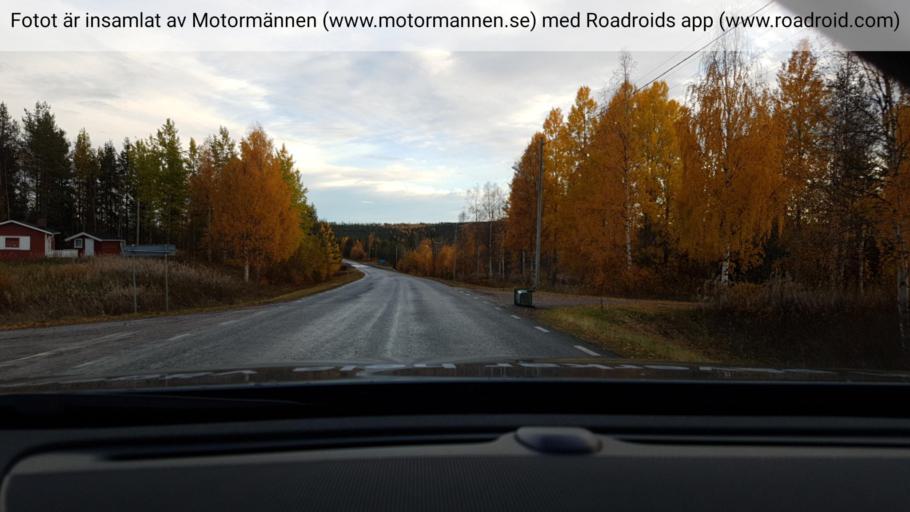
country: SE
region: Norrbotten
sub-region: Overkalix Kommun
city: OEverkalix
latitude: 66.9313
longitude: 22.7365
